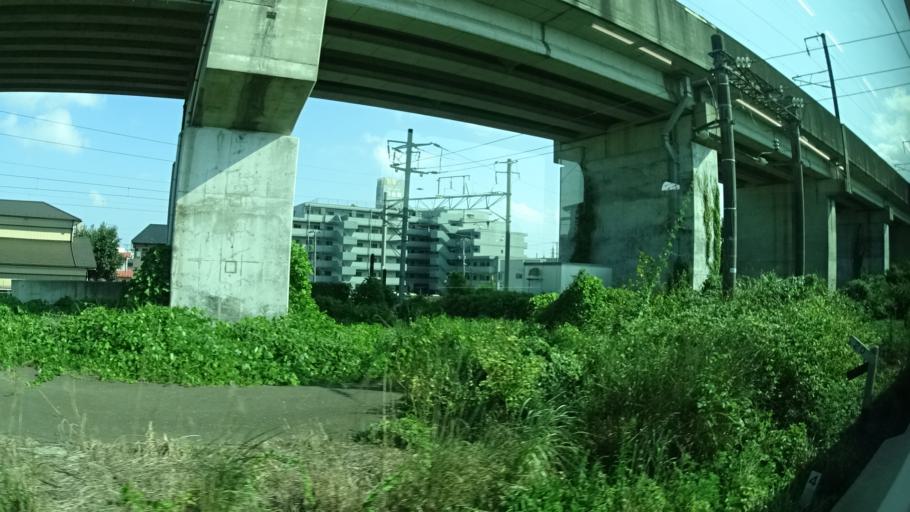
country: JP
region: Miyagi
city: Sendai-shi
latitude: 38.2726
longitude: 140.9137
